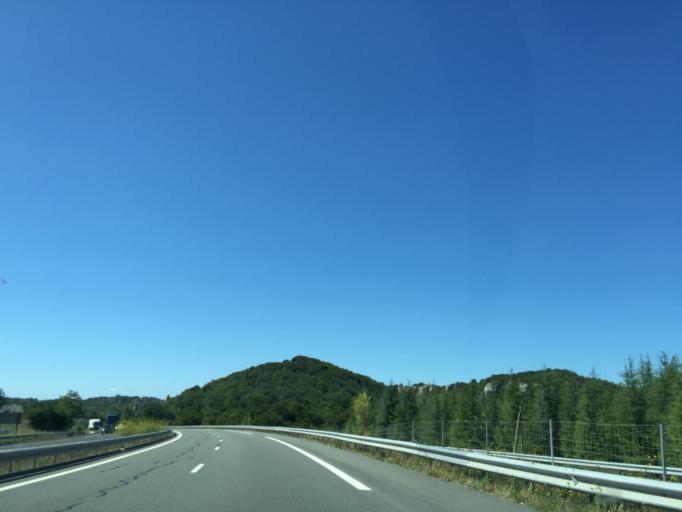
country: FR
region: Languedoc-Roussillon
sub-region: Departement de l'Herault
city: Lodeve
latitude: 43.8869
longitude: 3.2946
